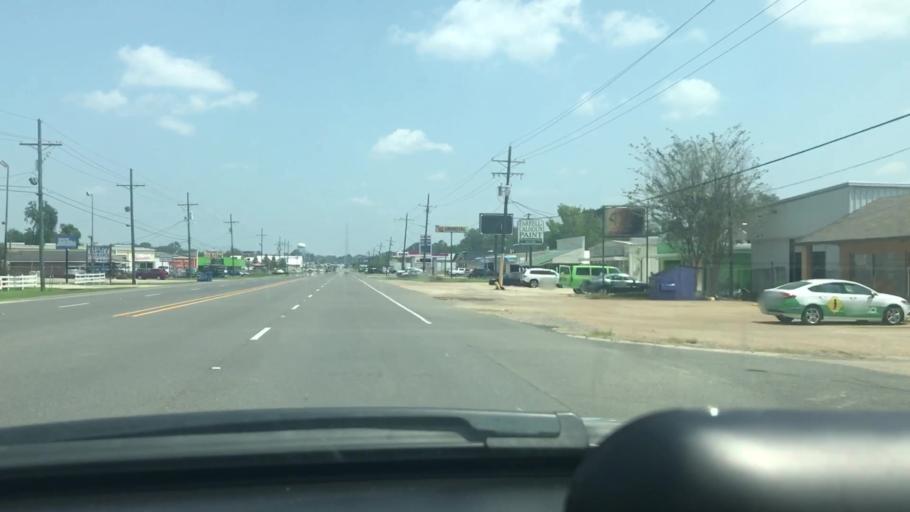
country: US
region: Louisiana
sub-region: Livingston Parish
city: Denham Springs
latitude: 30.4736
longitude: -90.9626
